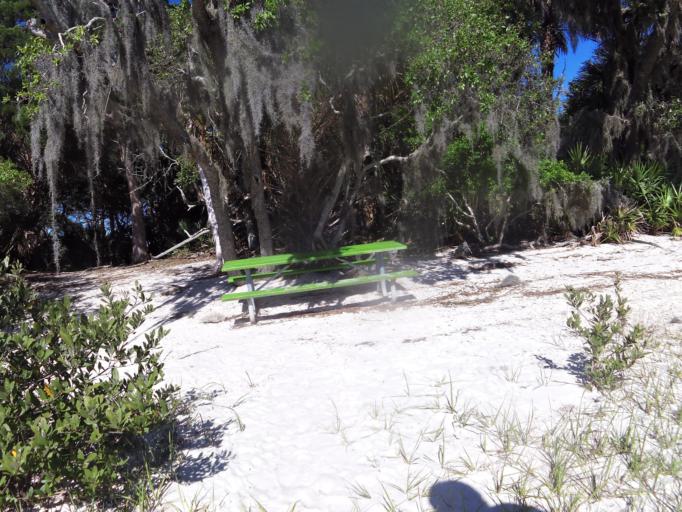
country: US
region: Florida
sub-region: Saint Johns County
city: Villano Beach
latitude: 29.9870
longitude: -81.3272
